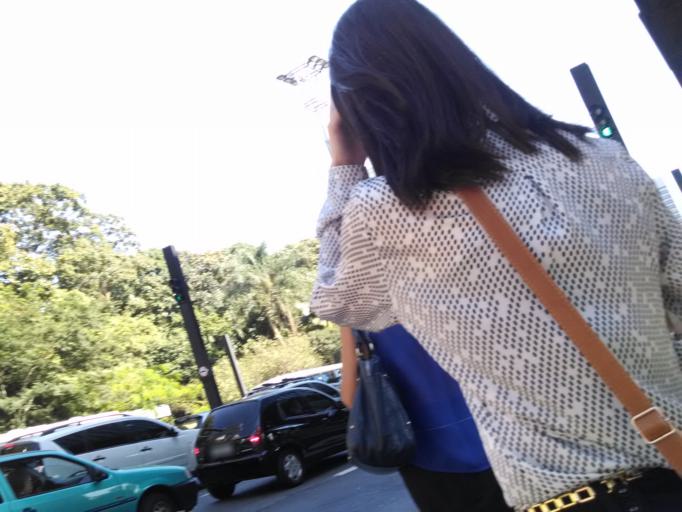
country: BR
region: Sao Paulo
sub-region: Sao Paulo
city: Sao Paulo
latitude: -23.5620
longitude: -46.6556
